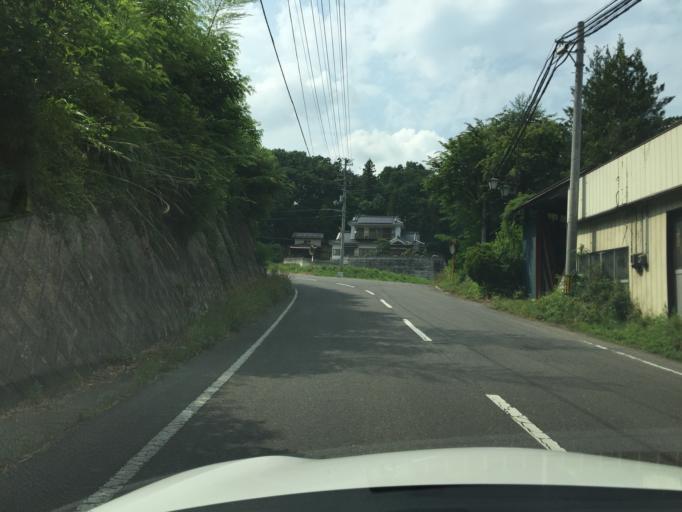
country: JP
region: Fukushima
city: Sukagawa
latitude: 37.2537
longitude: 140.4347
